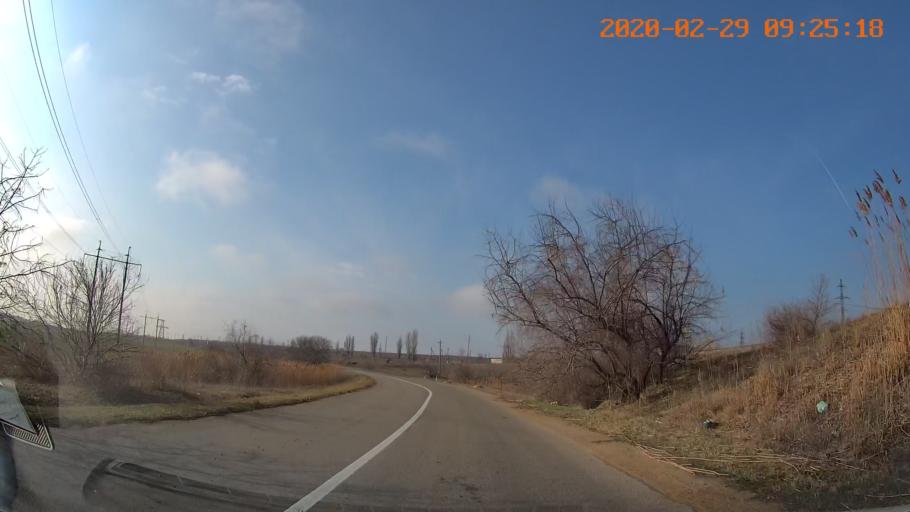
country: MD
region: Telenesti
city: Pervomaisc
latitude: 46.7098
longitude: 29.9535
